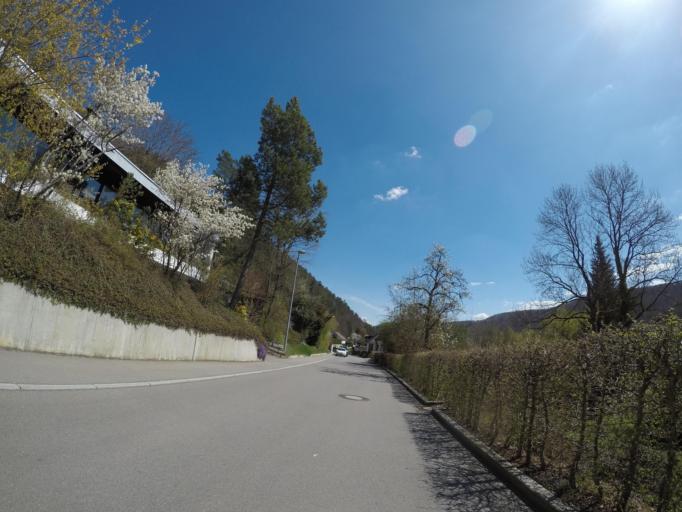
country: DE
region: Baden-Wuerttemberg
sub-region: Tuebingen Region
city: Blaubeuren
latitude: 48.4059
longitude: 9.7711
